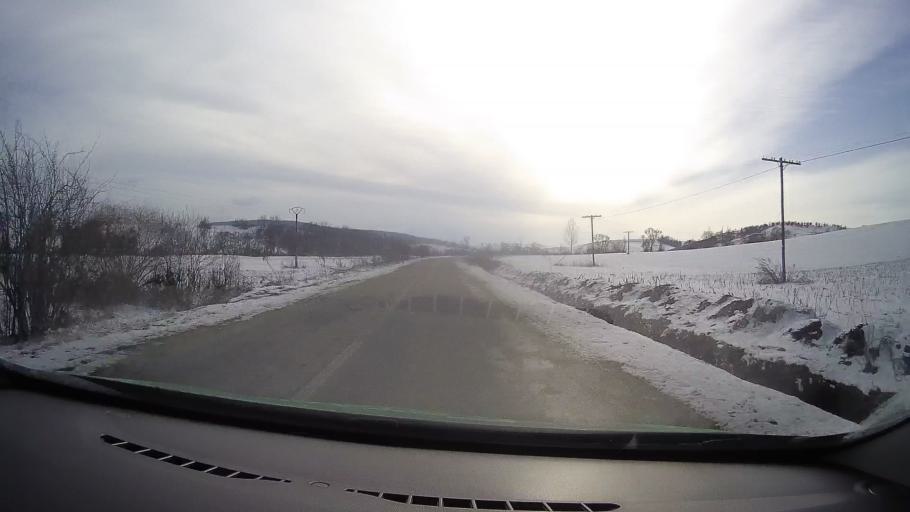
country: RO
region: Sibiu
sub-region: Oras Agnita
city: Ruja
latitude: 46.0081
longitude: 24.6820
